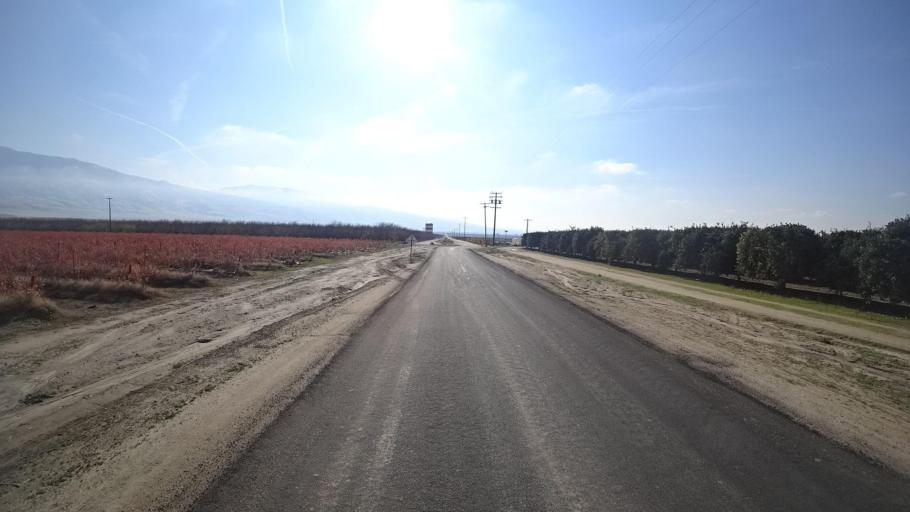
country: US
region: California
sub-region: Kern County
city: Arvin
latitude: 35.2683
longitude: -118.7707
